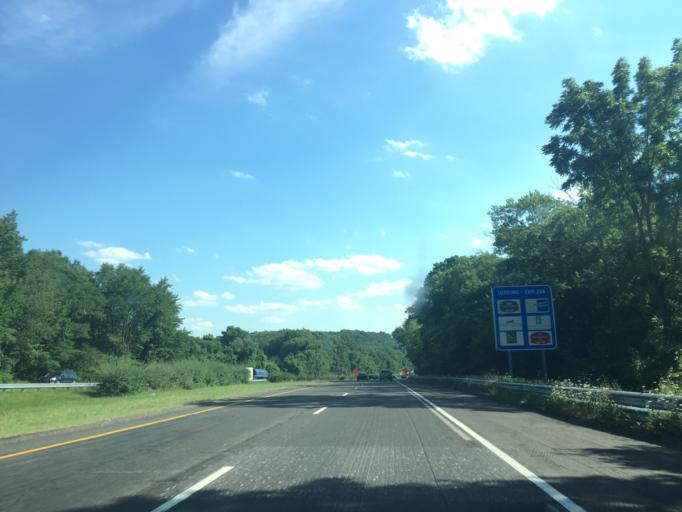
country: US
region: Maryland
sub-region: Baltimore County
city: Hunt Valley
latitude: 39.5189
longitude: -76.6619
